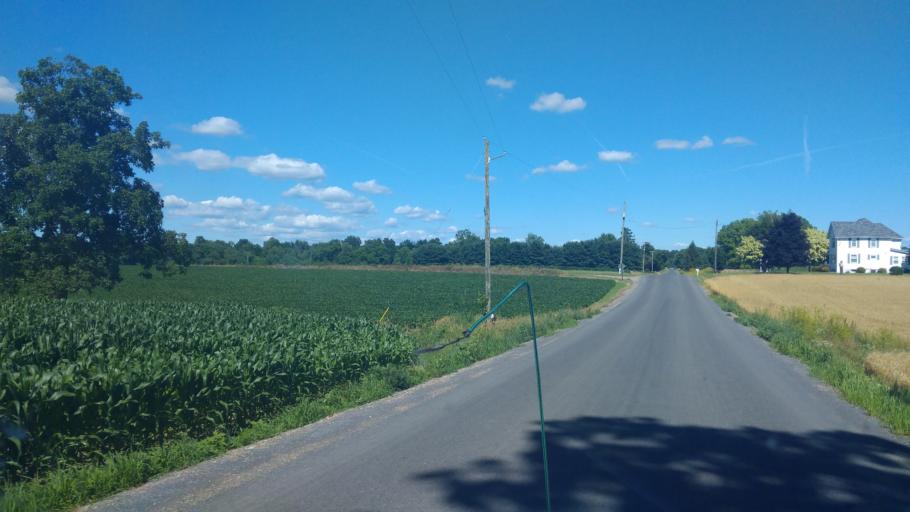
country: US
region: New York
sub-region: Wayne County
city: Clyde
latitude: 43.0261
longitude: -76.8935
